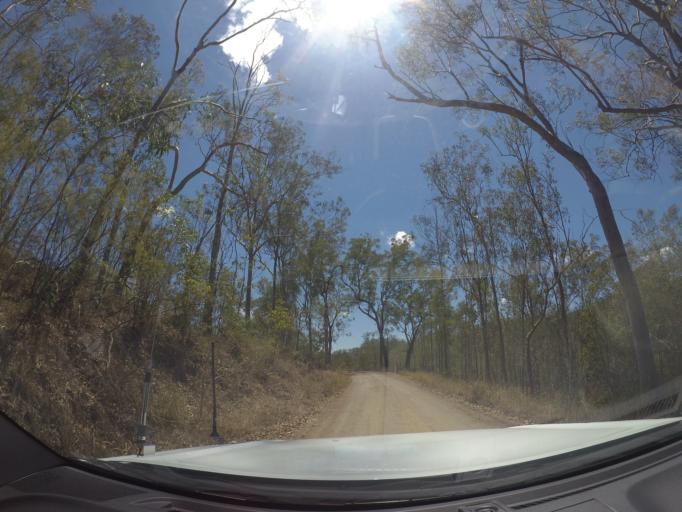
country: AU
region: Queensland
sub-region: Ipswich
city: Redbank Plains
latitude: -27.8030
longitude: 152.8434
